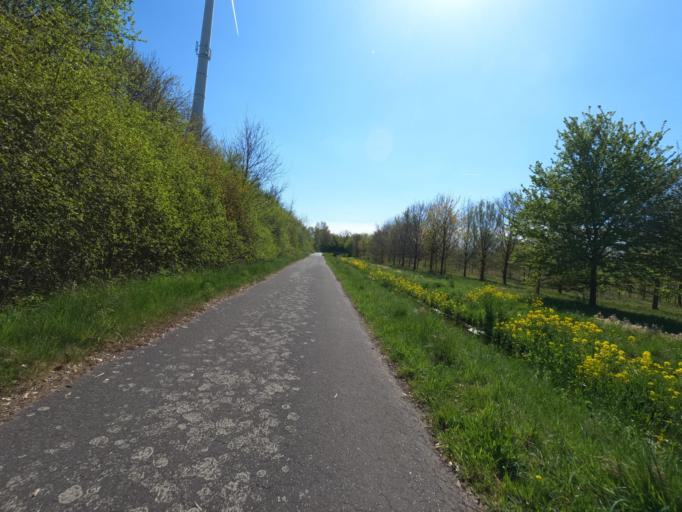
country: DE
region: North Rhine-Westphalia
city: Baesweiler
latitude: 50.9331
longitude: 6.2146
